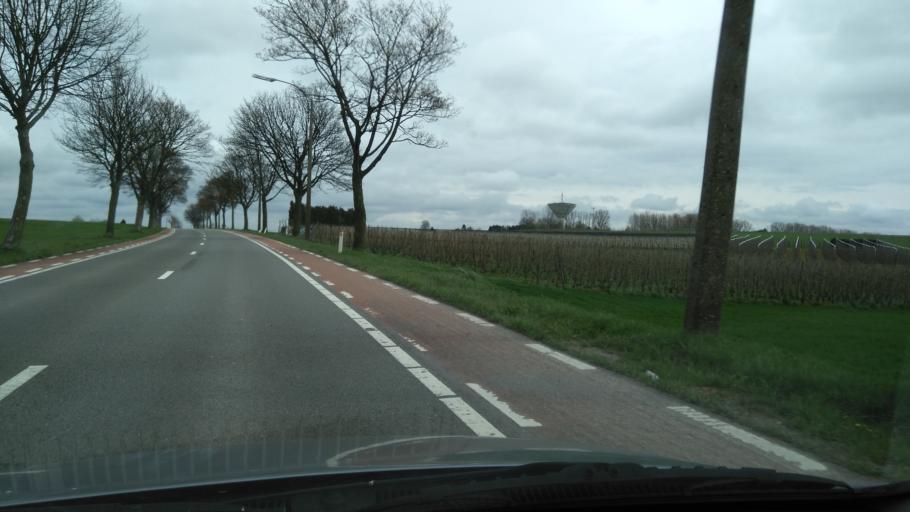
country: BE
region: Flanders
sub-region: Provincie Limburg
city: Bilzen
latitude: 50.8438
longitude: 5.5581
